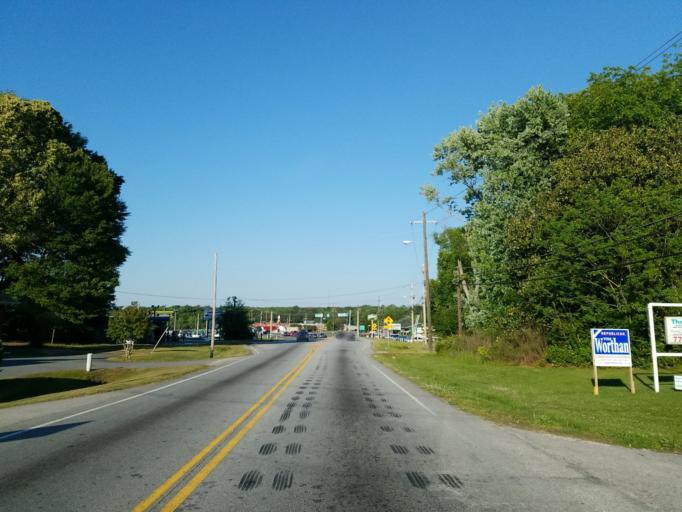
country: US
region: Georgia
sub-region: Douglas County
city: Lithia Springs
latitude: 33.7961
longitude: -84.6459
